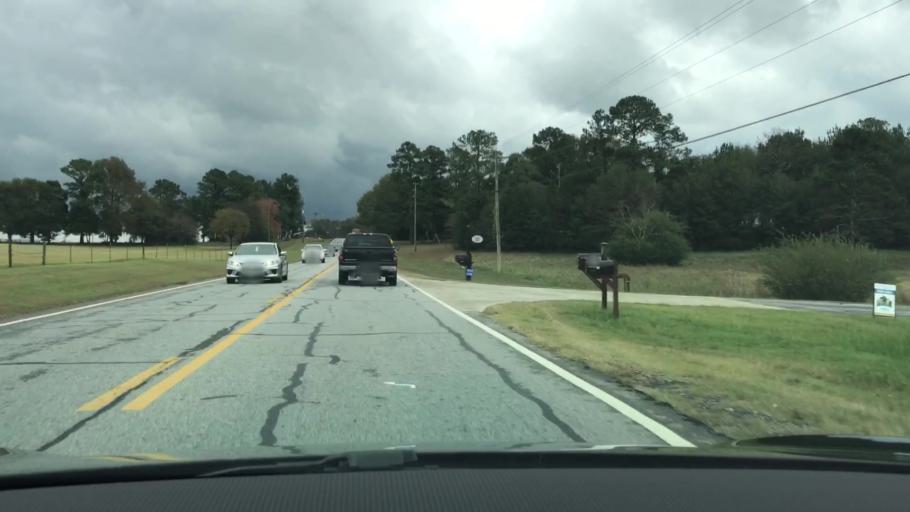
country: US
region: Georgia
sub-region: Oconee County
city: Watkinsville
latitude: 33.7929
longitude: -83.3254
